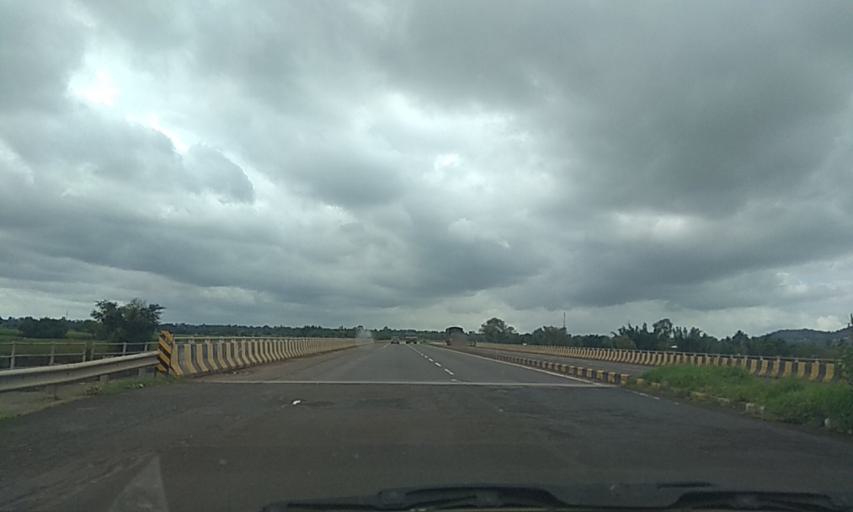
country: IN
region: Karnataka
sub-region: Belgaum
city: Sankeshwar
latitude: 16.2480
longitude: 74.4819
